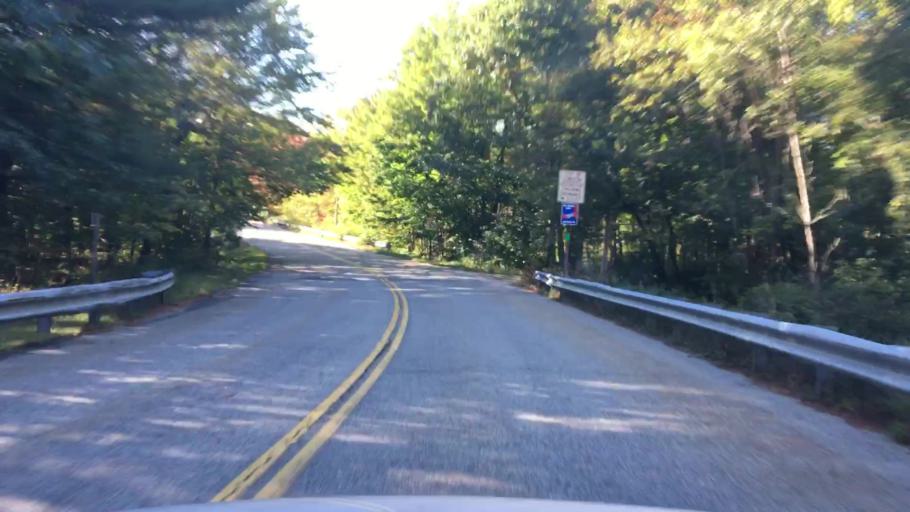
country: US
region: Maine
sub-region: Androscoggin County
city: Lisbon
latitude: 44.0719
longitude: -70.1397
